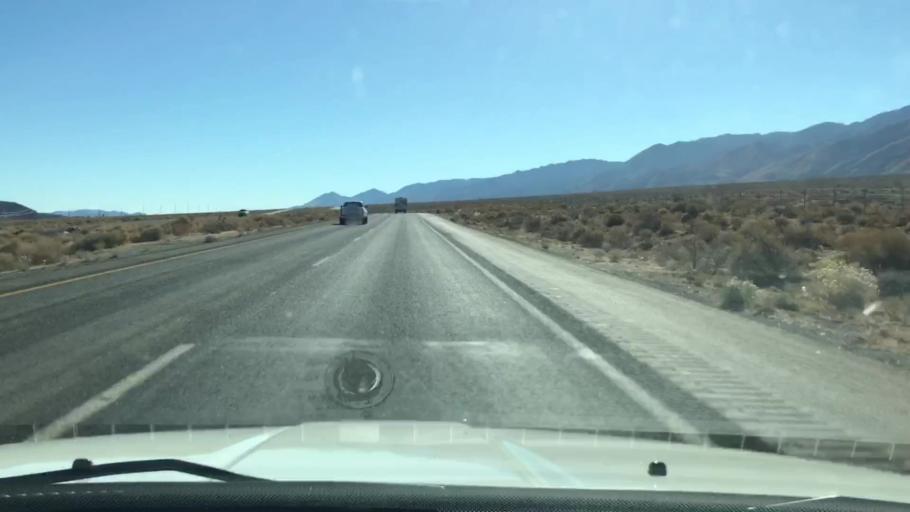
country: US
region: California
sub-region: Inyo County
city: Lone Pine
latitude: 36.1664
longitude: -117.9782
